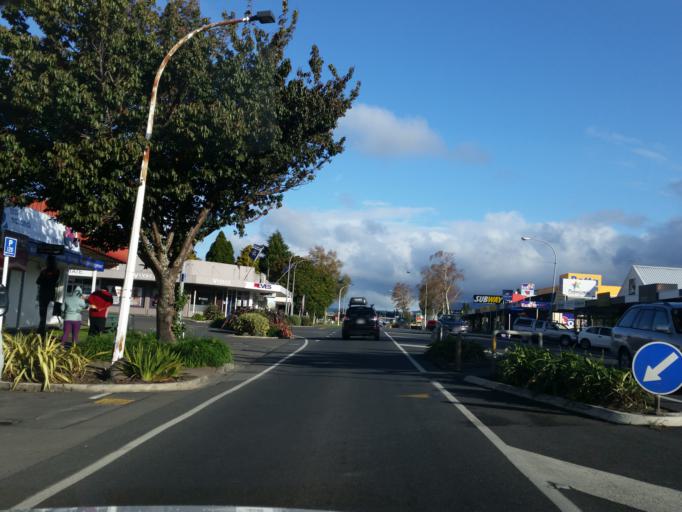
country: NZ
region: Bay of Plenty
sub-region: Western Bay of Plenty District
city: Katikati
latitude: -37.5540
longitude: 175.9172
